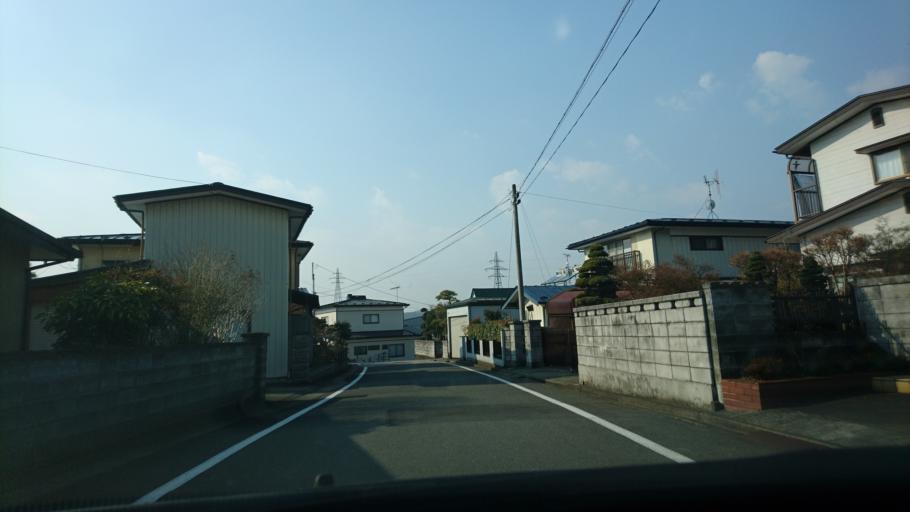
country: JP
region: Iwate
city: Ichinoseki
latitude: 38.9861
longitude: 141.1129
